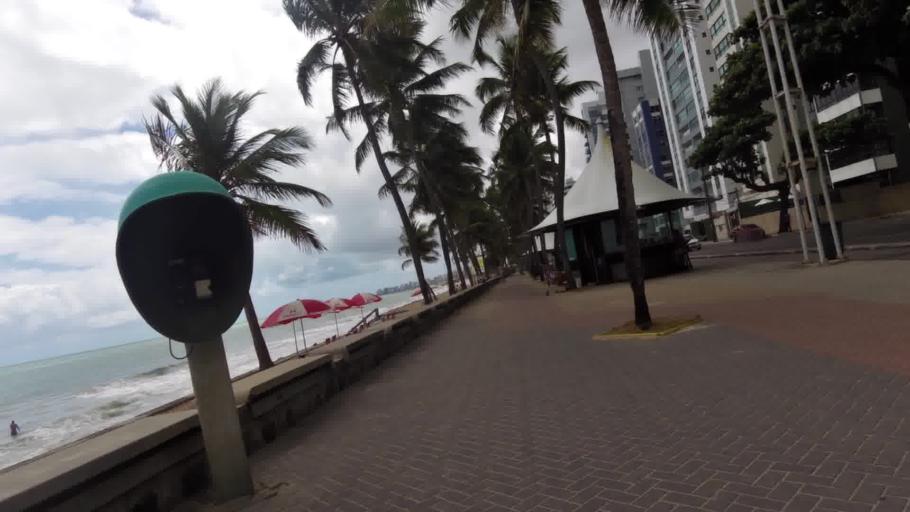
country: BR
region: Pernambuco
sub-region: Recife
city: Recife
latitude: -8.1439
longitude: -34.9044
